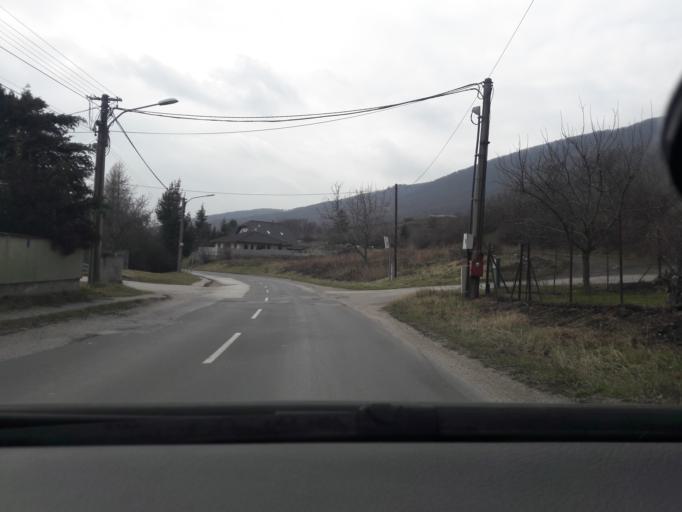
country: SK
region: Trnavsky
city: Smolenice
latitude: 48.4595
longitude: 17.4316
